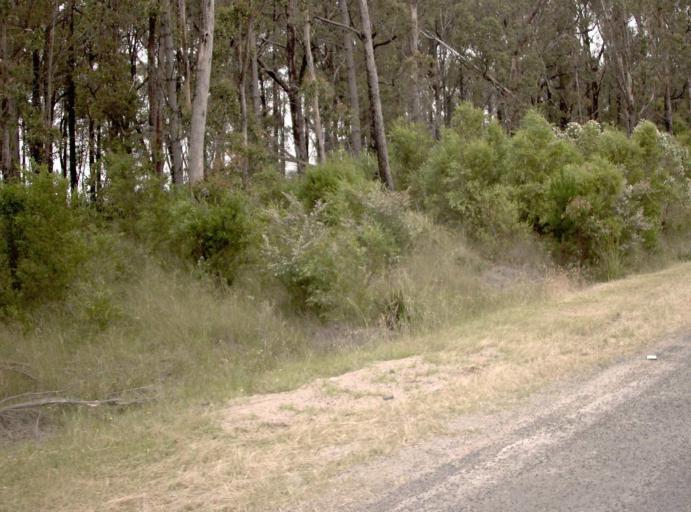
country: AU
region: Victoria
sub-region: Latrobe
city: Moe
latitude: -38.3156
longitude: 146.2644
